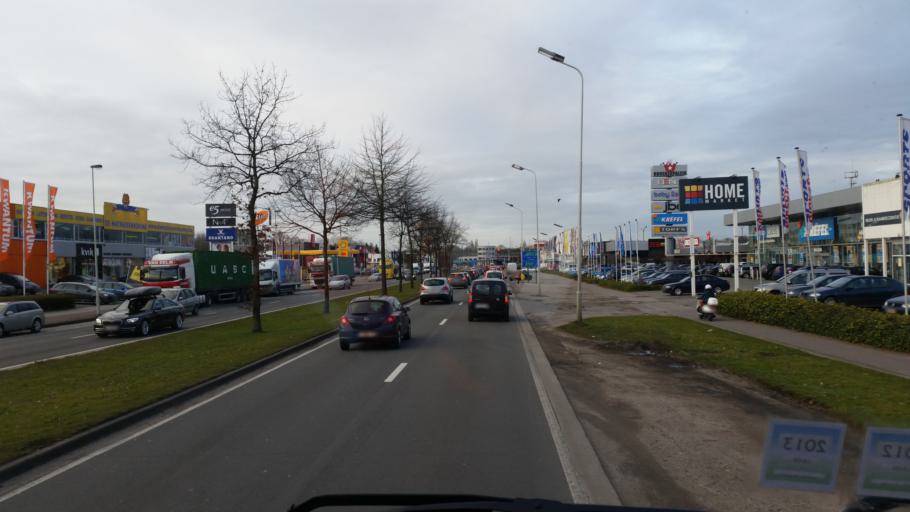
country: BE
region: Flanders
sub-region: Provincie Antwerpen
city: Brasschaat
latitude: 51.2631
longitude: 4.4637
